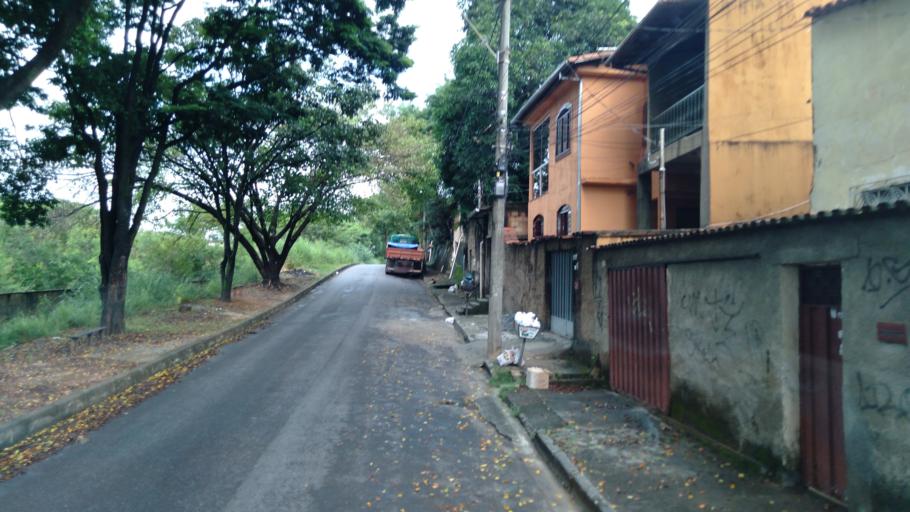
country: BR
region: Minas Gerais
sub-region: Belo Horizonte
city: Belo Horizonte
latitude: -19.9020
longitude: -43.9020
